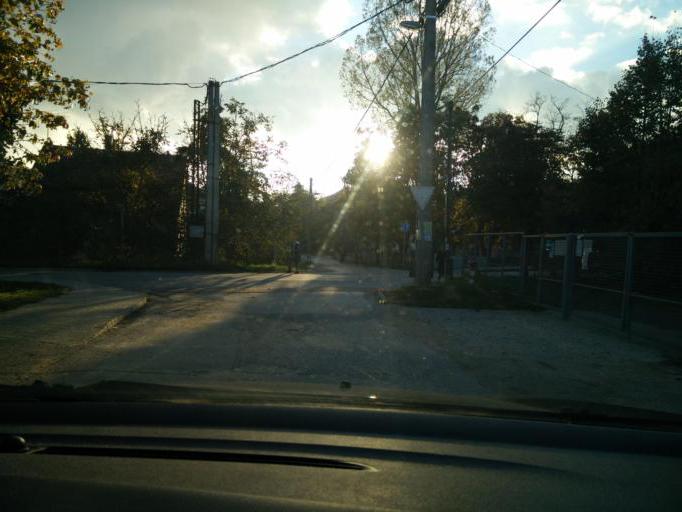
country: HU
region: Pest
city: Piliscsaba
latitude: 47.6343
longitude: 18.8429
